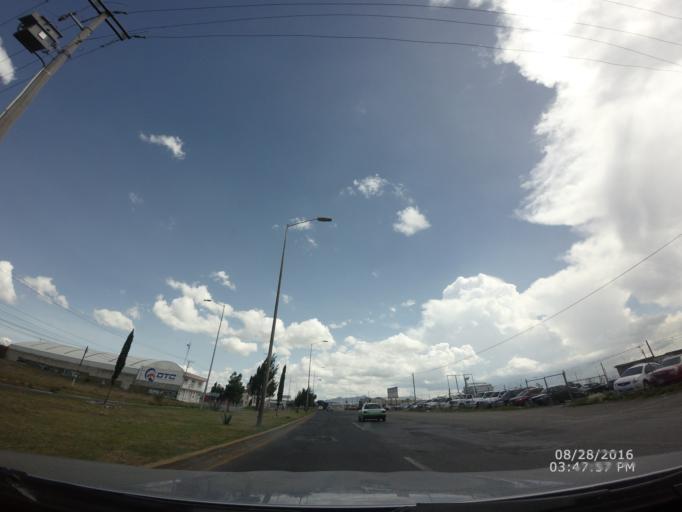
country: MX
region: Hidalgo
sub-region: Mineral de la Reforma
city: Nuevo Centro de Poblacion Agricola el Chacon
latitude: 20.0617
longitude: -98.7441
